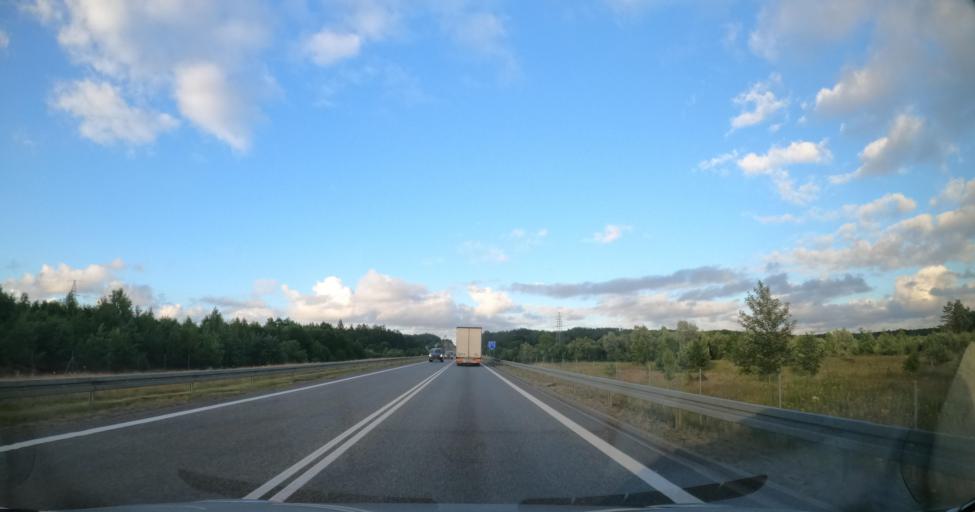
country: PL
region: Pomeranian Voivodeship
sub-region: Powiat slupski
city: Kobylnica
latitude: 54.4268
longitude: 17.0242
